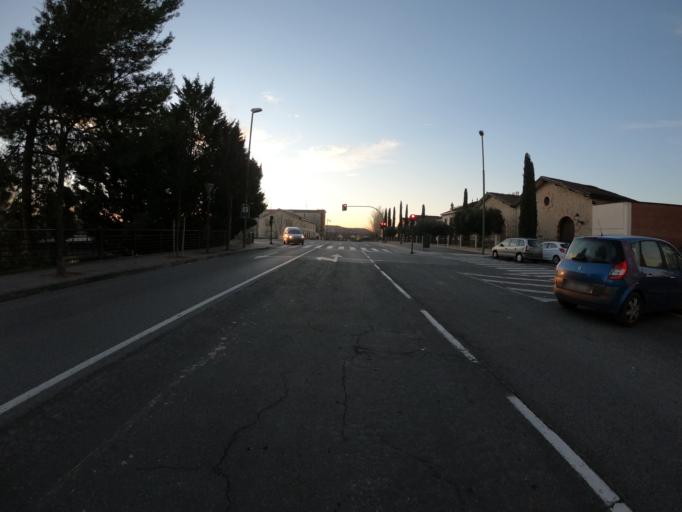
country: ES
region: La Rioja
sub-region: Provincia de La Rioja
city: Logrono
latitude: 42.4715
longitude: -2.4464
